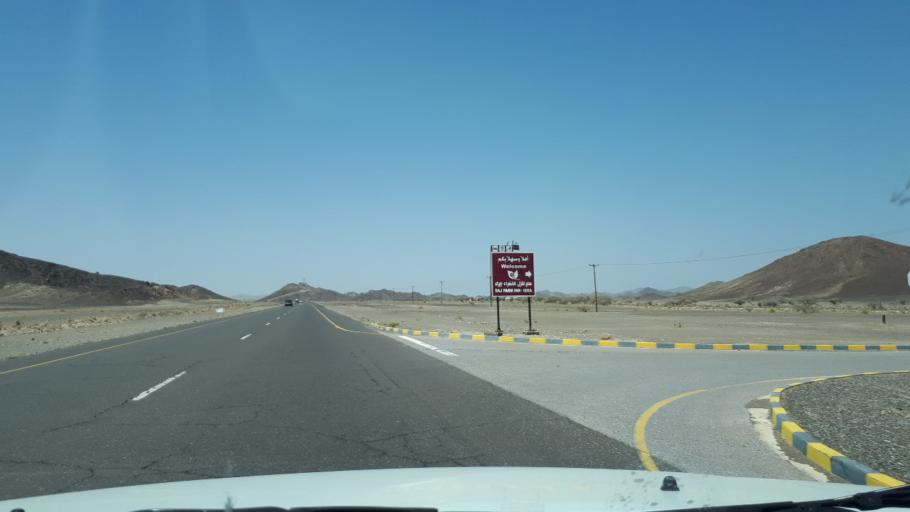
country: OM
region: Ash Sharqiyah
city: Ibra'
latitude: 22.6350
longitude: 58.4701
